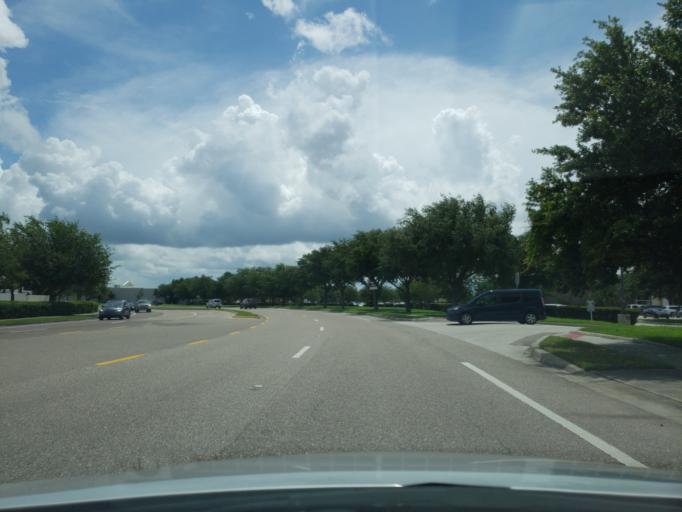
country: US
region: Florida
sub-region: Hillsborough County
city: Progress Village
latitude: 27.9204
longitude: -82.3286
